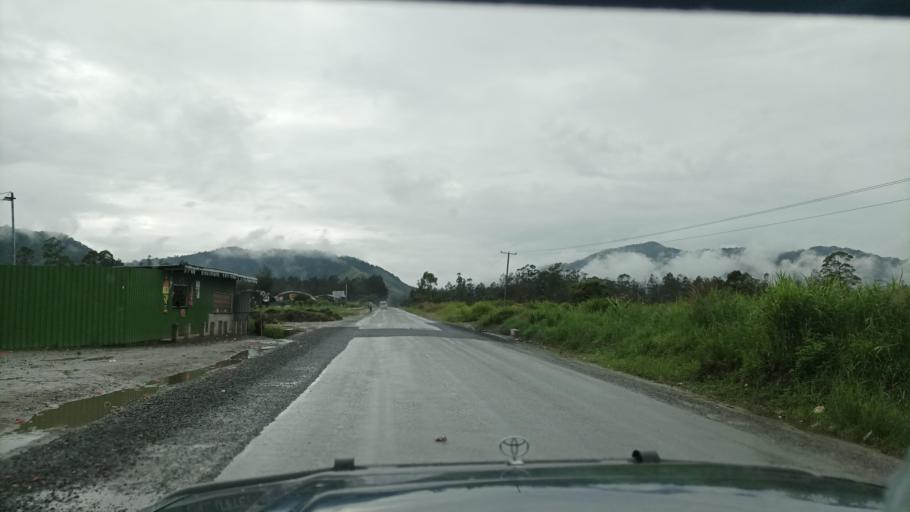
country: PG
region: Western Highlands
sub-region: Hagen
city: Mount Hagen
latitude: -5.8373
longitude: 144.3303
